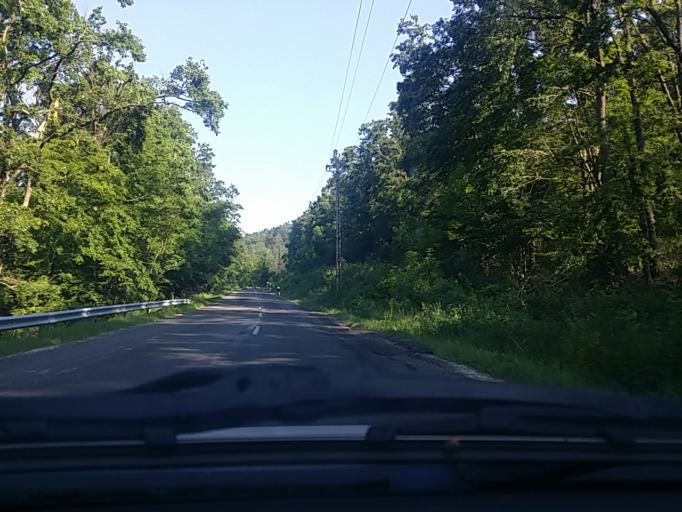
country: HU
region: Pest
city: Pilisszentkereszt
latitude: 47.7094
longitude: 18.8813
